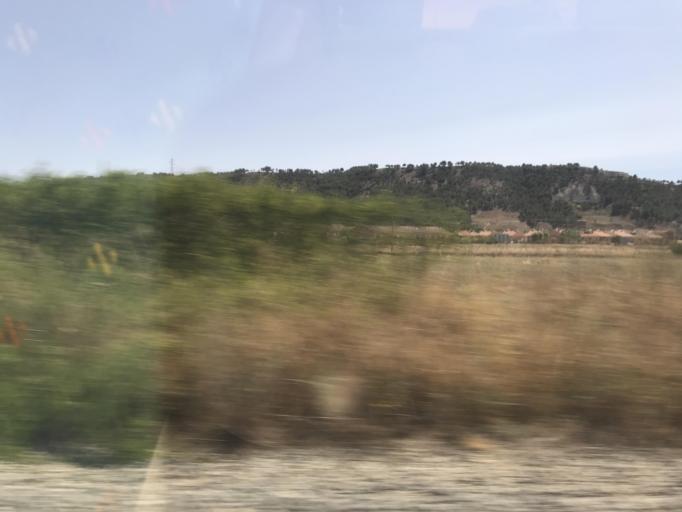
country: ES
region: Castille and Leon
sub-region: Provincia de Valladolid
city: Cabezon
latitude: 41.7453
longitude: -4.6439
